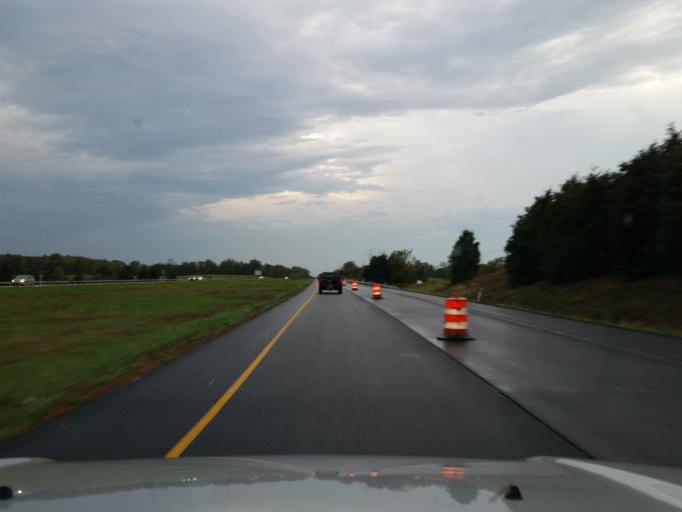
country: US
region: Pennsylvania
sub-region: Adams County
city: Lake Heritage
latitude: 39.7857
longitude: -77.2184
